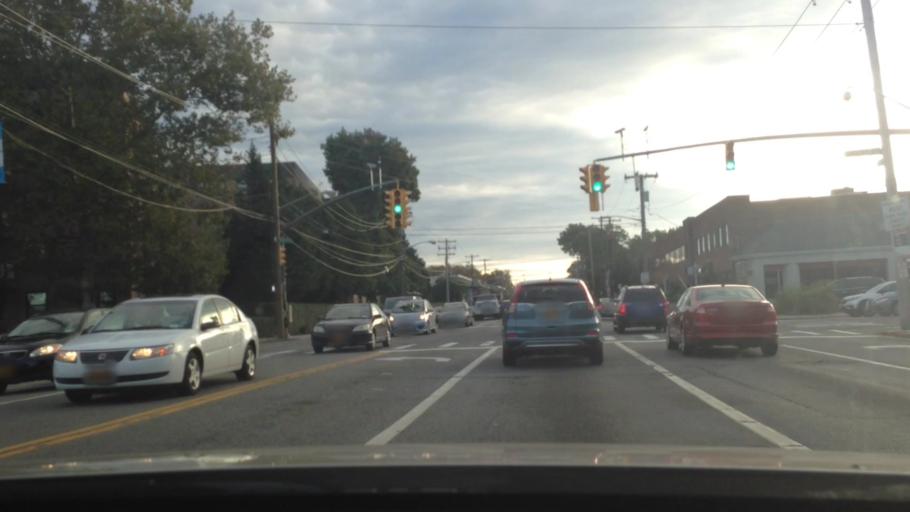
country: US
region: New York
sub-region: Nassau County
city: Mineola
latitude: 40.7400
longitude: -73.6336
